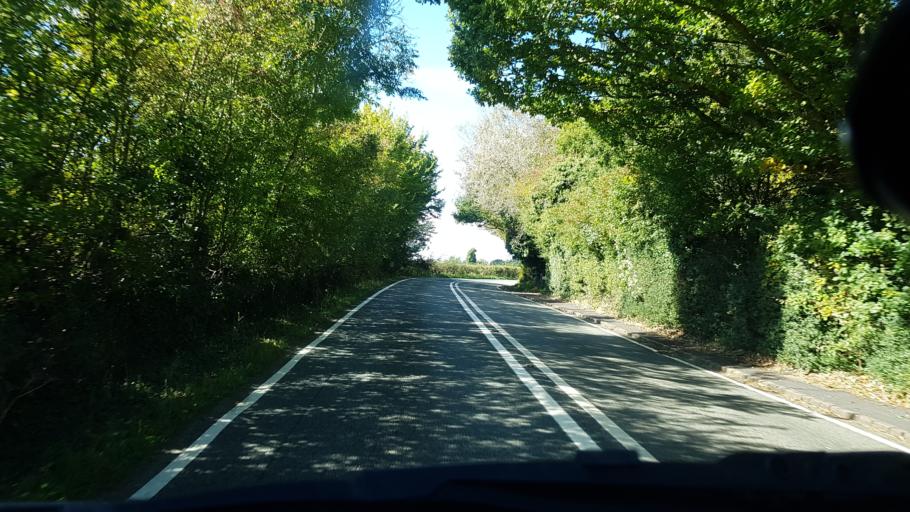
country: GB
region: England
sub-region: West Sussex
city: Billingshurst
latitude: 51.0193
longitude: -0.4956
